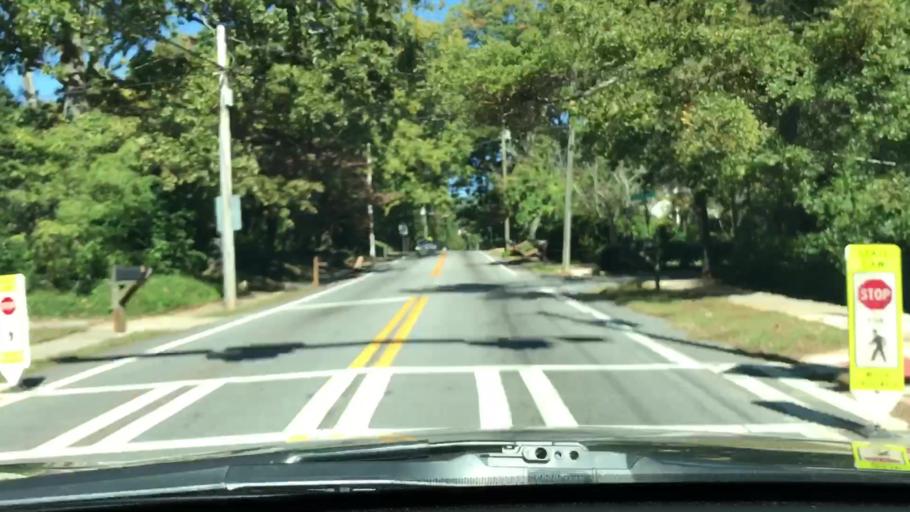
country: US
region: Georgia
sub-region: DeKalb County
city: Decatur
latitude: 33.7636
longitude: -84.2925
